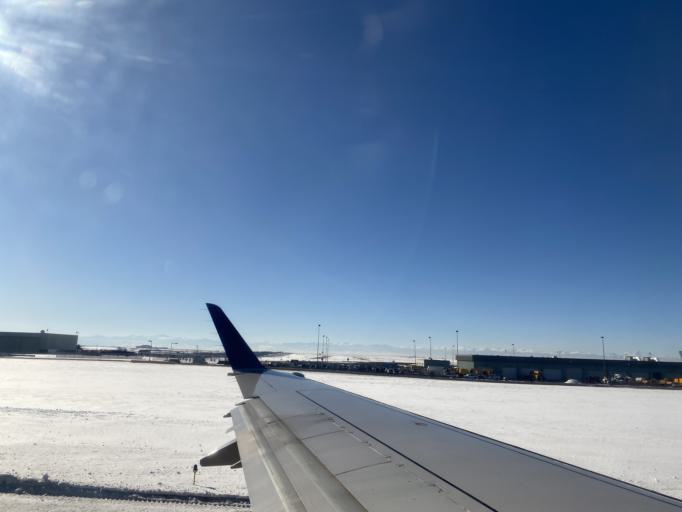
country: US
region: Colorado
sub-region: Weld County
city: Lochbuie
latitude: 39.8412
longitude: -104.6625
